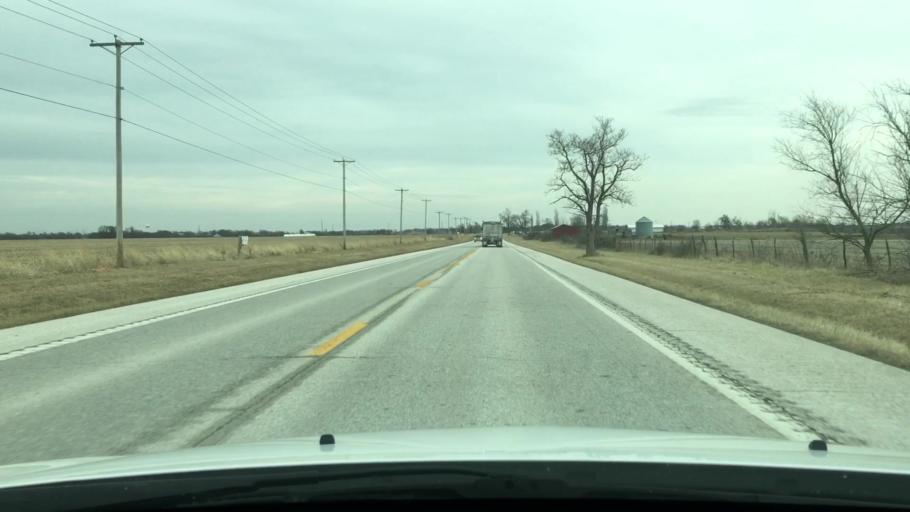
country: US
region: Missouri
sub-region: Pike County
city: Bowling Green
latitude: 39.3443
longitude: -91.2624
